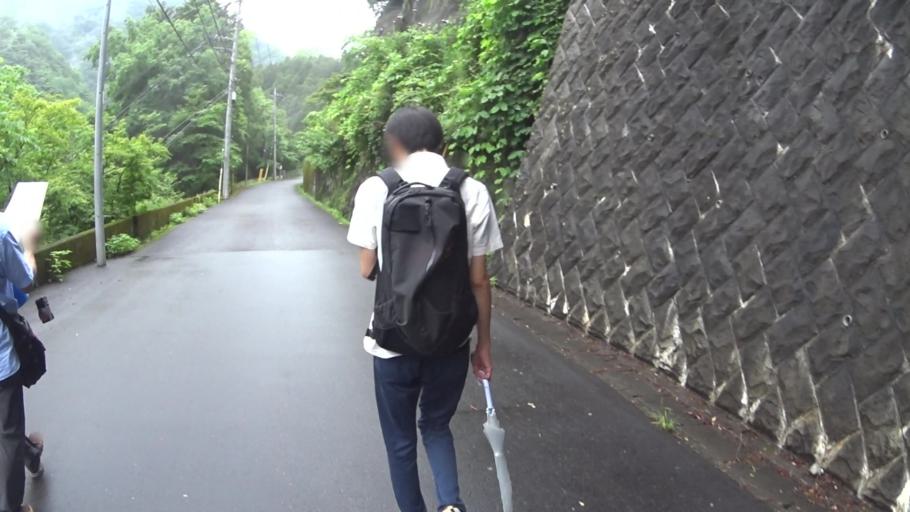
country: JP
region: Tokyo
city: Itsukaichi
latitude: 35.7933
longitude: 139.0589
